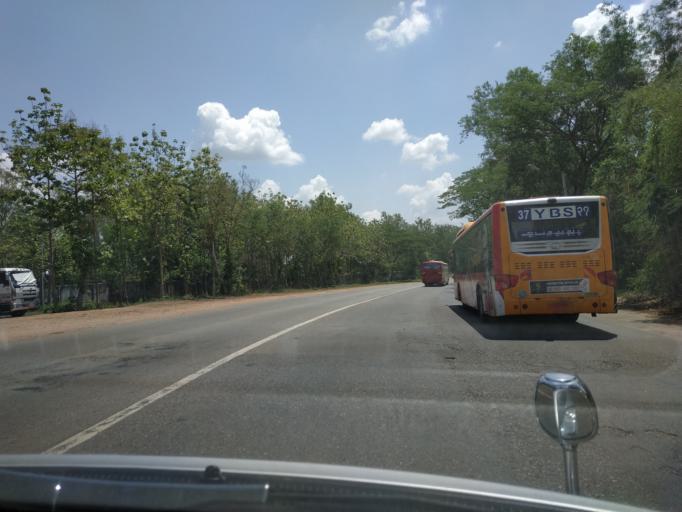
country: MM
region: Yangon
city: Yangon
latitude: 16.9885
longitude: 96.1277
